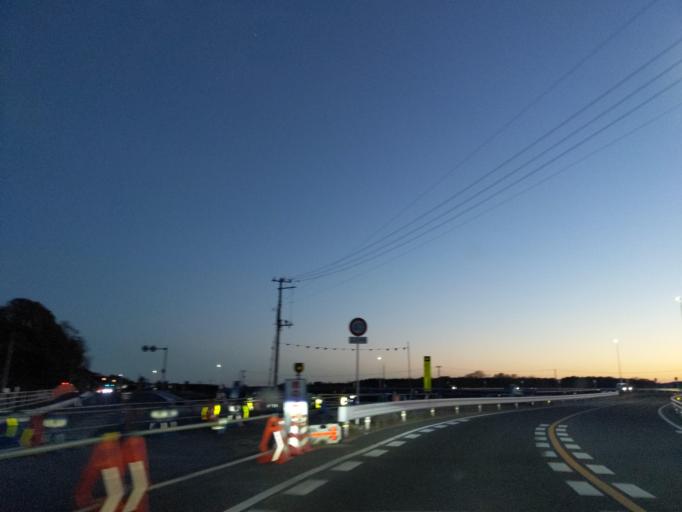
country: JP
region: Fukushima
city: Koriyama
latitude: 37.3554
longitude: 140.3966
